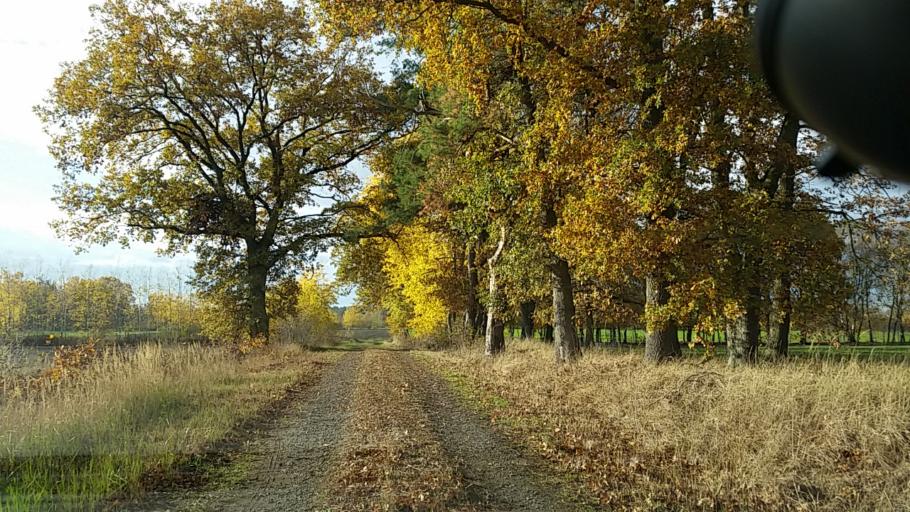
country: DE
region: Lower Saxony
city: Ruhen
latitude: 52.4598
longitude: 10.8317
